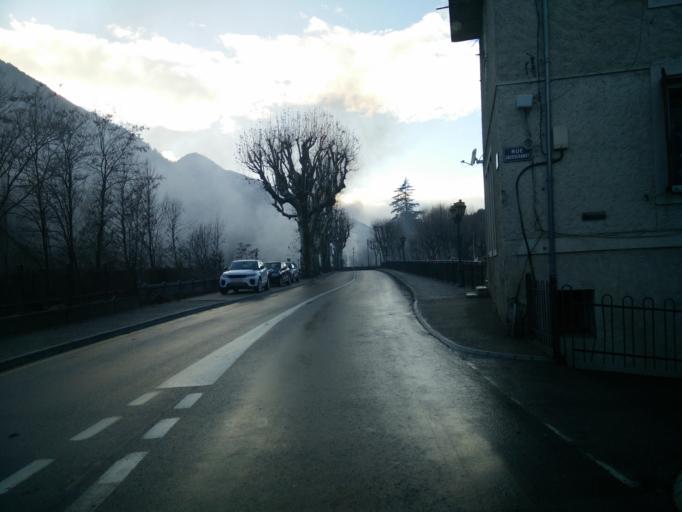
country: FR
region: Provence-Alpes-Cote d'Azur
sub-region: Departement des Alpes-Maritimes
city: Puget-Theniers
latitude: 43.9551
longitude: 6.8952
